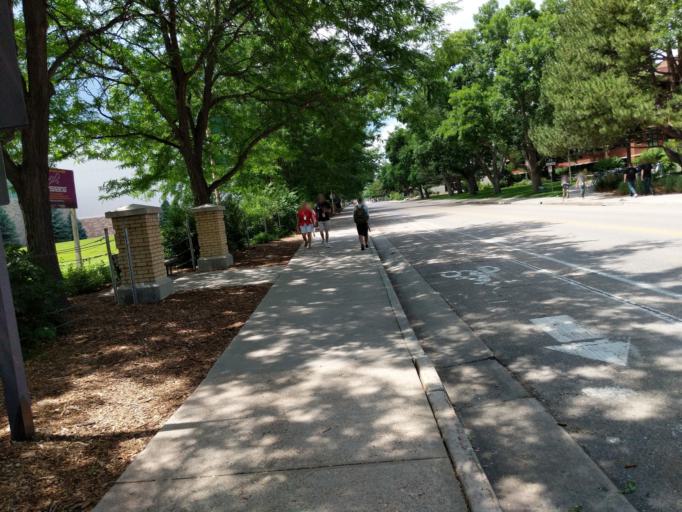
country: US
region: Colorado
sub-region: Larimer County
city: Fort Collins
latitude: 40.5764
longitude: -105.0882
